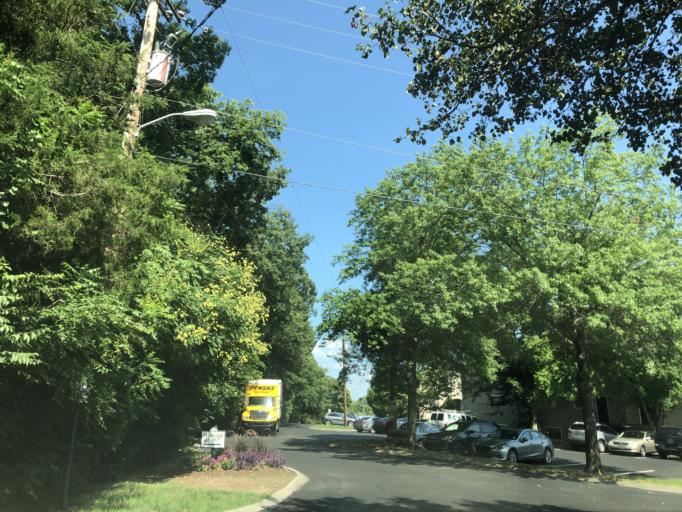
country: US
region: Tennessee
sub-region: Davidson County
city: Lakewood
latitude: 36.1451
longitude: -86.6226
